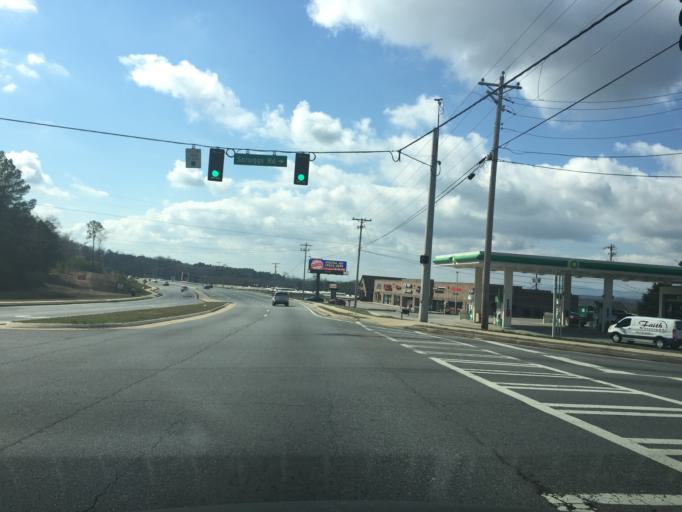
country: US
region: Georgia
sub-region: Catoosa County
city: Indian Springs
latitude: 34.9659
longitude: -85.1934
